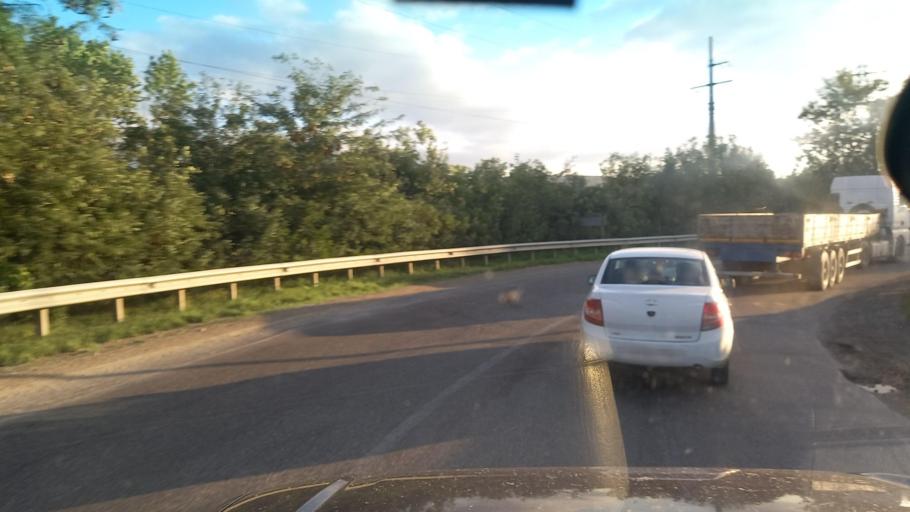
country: RU
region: Krasnodarskiy
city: Krymsk
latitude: 44.9010
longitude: 37.9826
